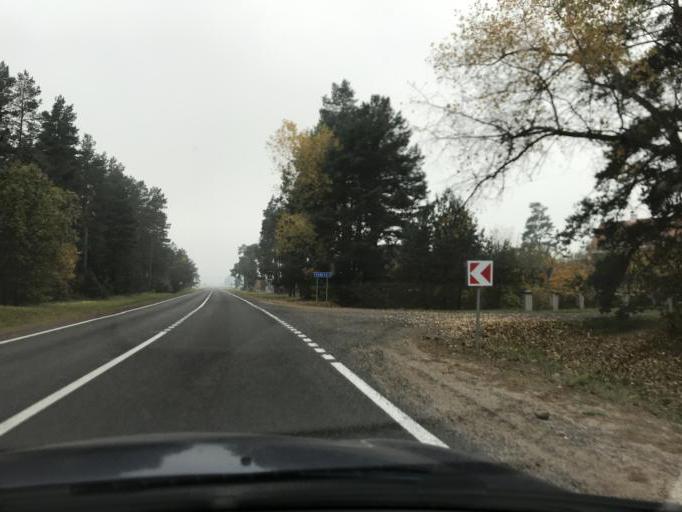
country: BY
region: Grodnenskaya
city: Hrodna
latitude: 53.8323
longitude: 23.8864
